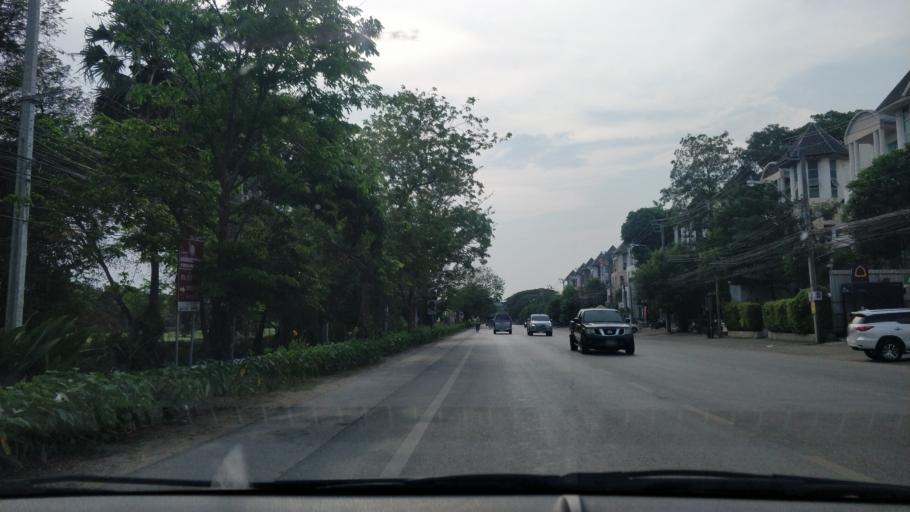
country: TH
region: Bangkok
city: Suan Luang
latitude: 13.7454
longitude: 100.6689
